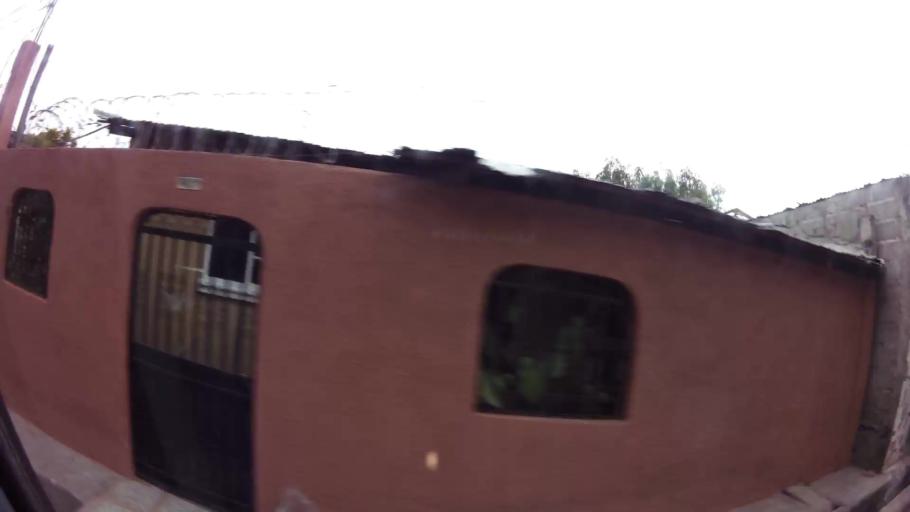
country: HN
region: Francisco Morazan
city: Tegucigalpa
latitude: 14.0982
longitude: -87.1727
